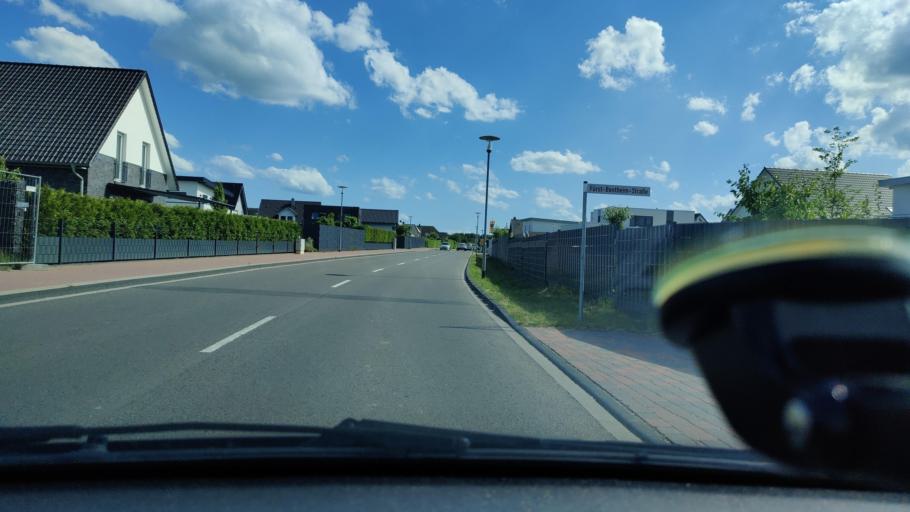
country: DE
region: North Rhine-Westphalia
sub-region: Regierungsbezirk Dusseldorf
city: Alpen
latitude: 51.5769
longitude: 6.5220
